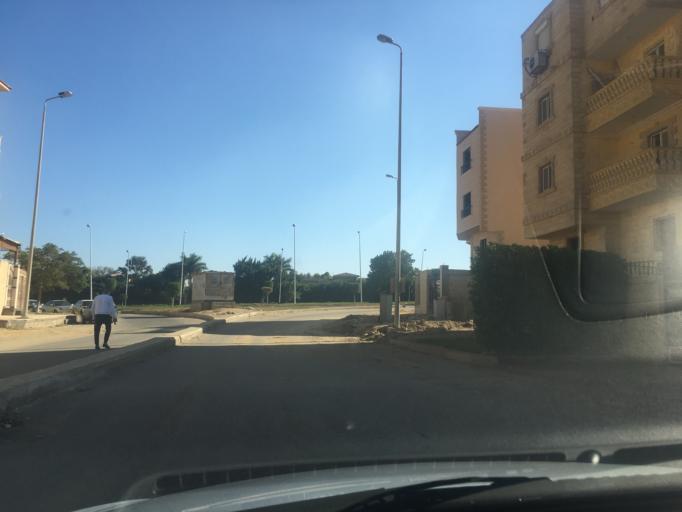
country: EG
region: Al Jizah
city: Awsim
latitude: 30.0256
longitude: 30.9850
